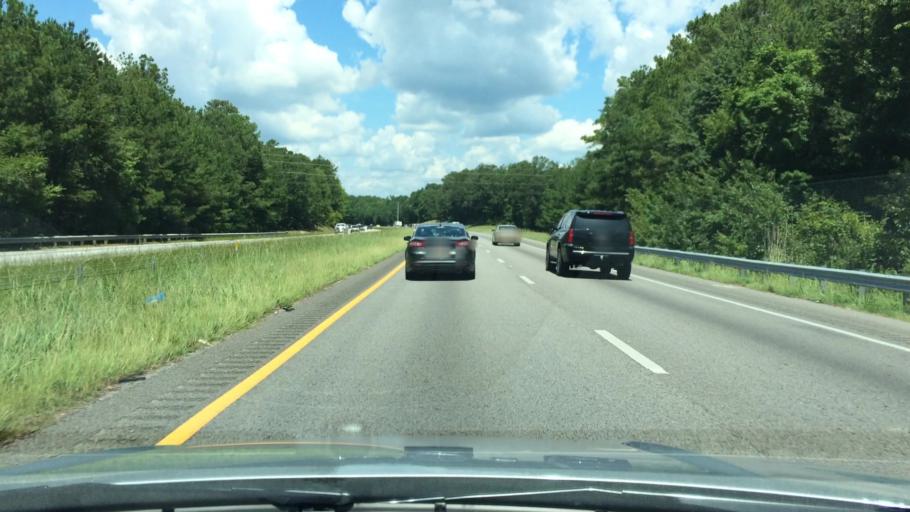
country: US
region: South Carolina
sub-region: Lexington County
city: Irmo
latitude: 34.1308
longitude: -81.2075
